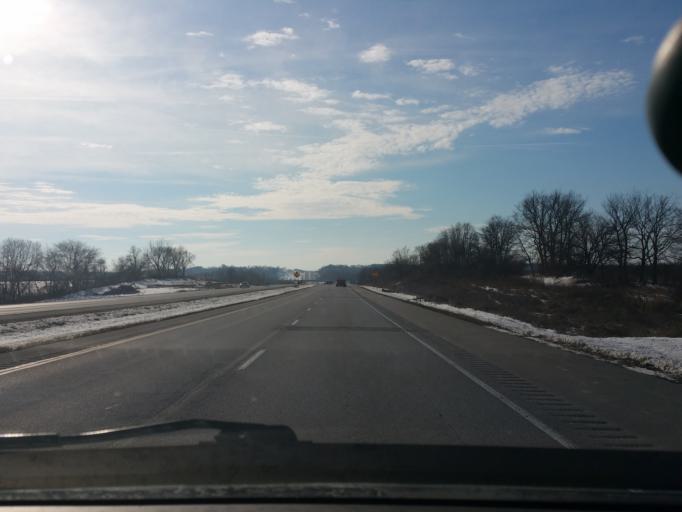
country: US
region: Iowa
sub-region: Warren County
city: Norwalk
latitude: 41.3742
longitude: -93.7809
